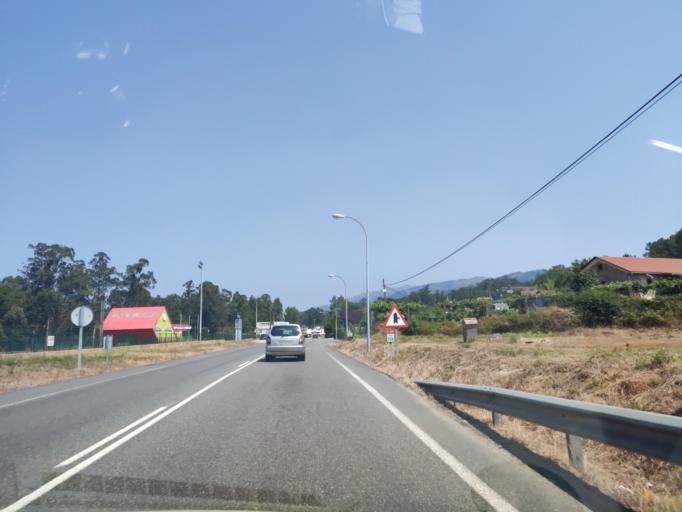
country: ES
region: Galicia
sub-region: Provincia de Pontevedra
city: Porrino
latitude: 42.1761
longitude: -8.6165
